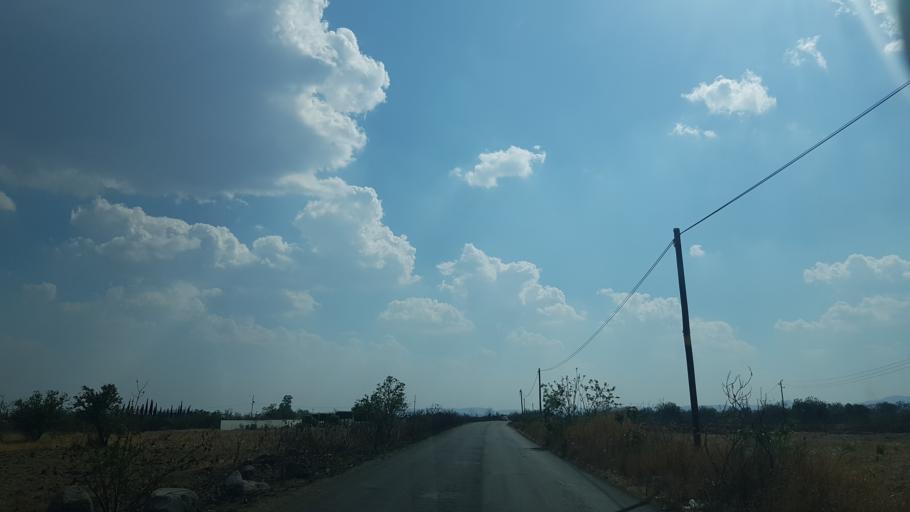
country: MX
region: Puebla
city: Atlixco
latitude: 18.9047
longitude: -98.4829
